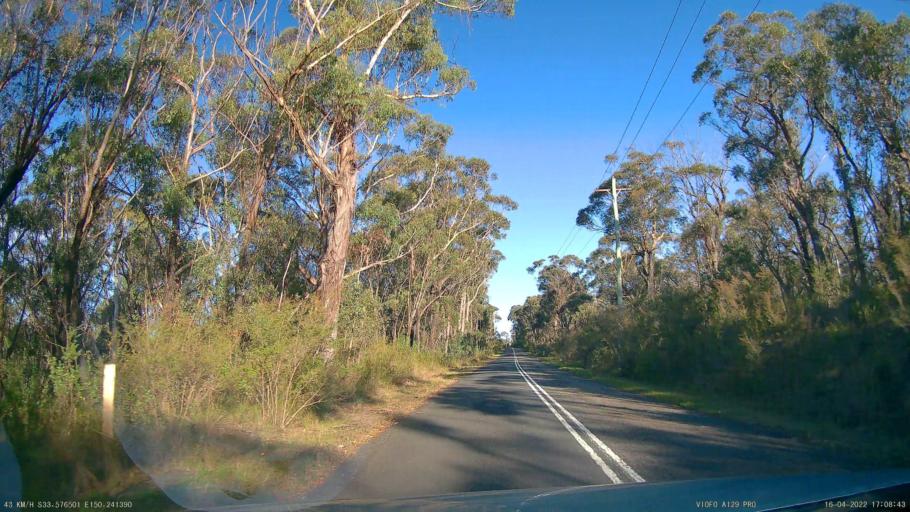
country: AU
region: New South Wales
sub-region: Blue Mountains Municipality
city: Blackheath
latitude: -33.5766
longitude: 150.2415
